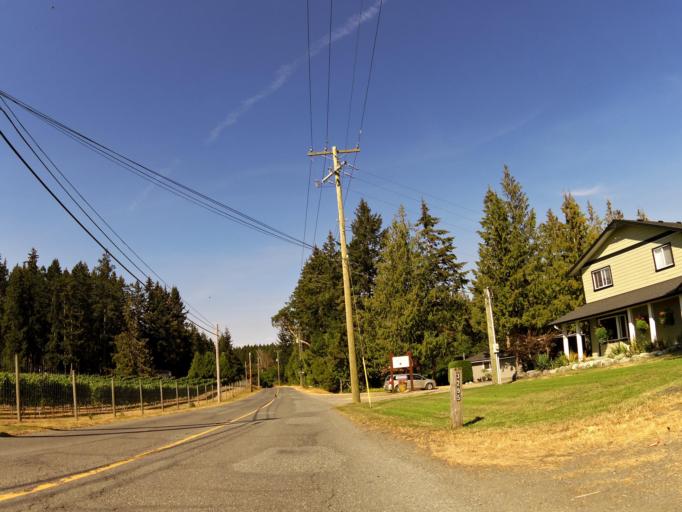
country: CA
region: British Columbia
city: North Saanich
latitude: 48.6771
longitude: -123.5509
